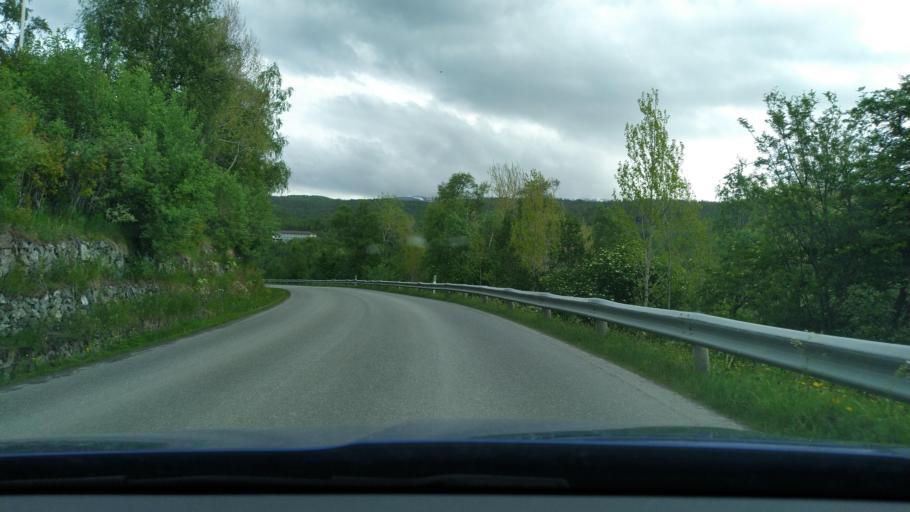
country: NO
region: Troms
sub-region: Salangen
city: Sjovegan
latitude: 68.8677
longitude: 17.8532
